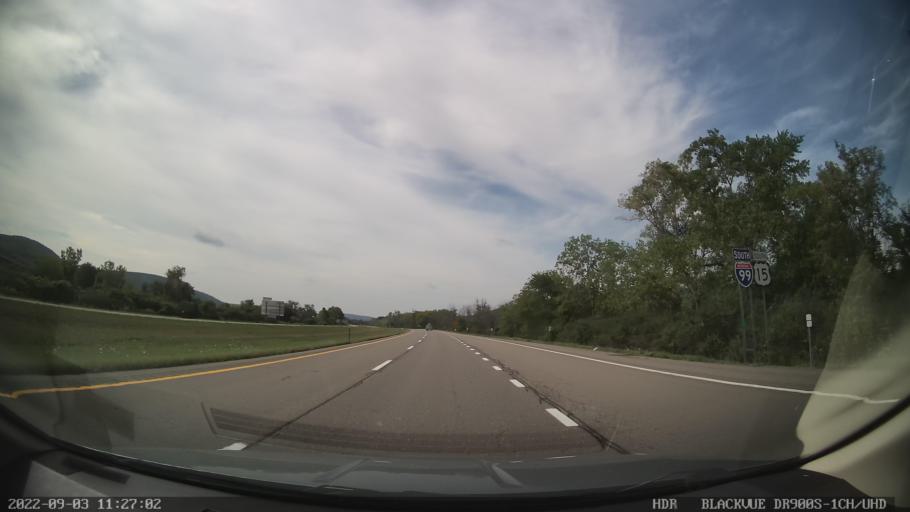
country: US
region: New York
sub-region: Steuben County
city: Gang Mills
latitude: 42.1387
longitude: -77.1216
